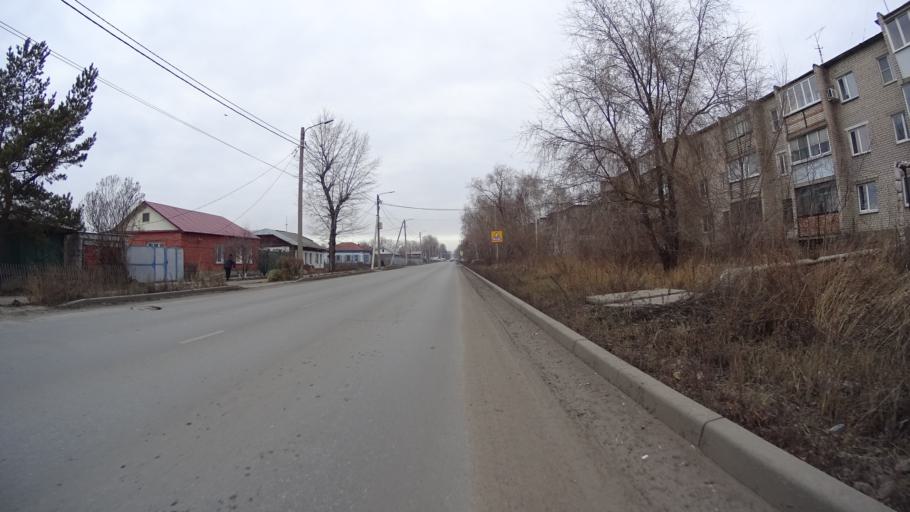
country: RU
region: Chelyabinsk
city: Troitsk
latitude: 54.1087
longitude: 61.5715
